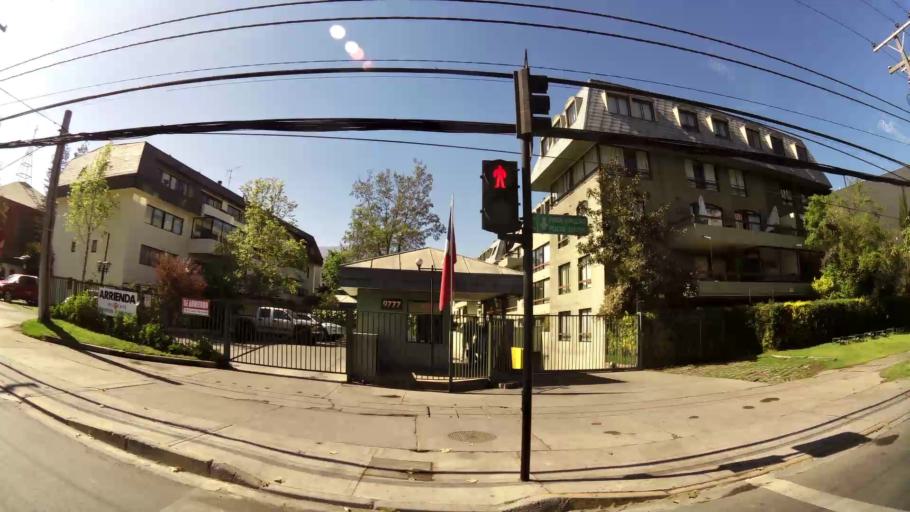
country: CL
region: Santiago Metropolitan
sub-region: Provincia de Santiago
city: Villa Presidente Frei, Nunoa, Santiago, Chile
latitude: -33.3865
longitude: -70.5379
